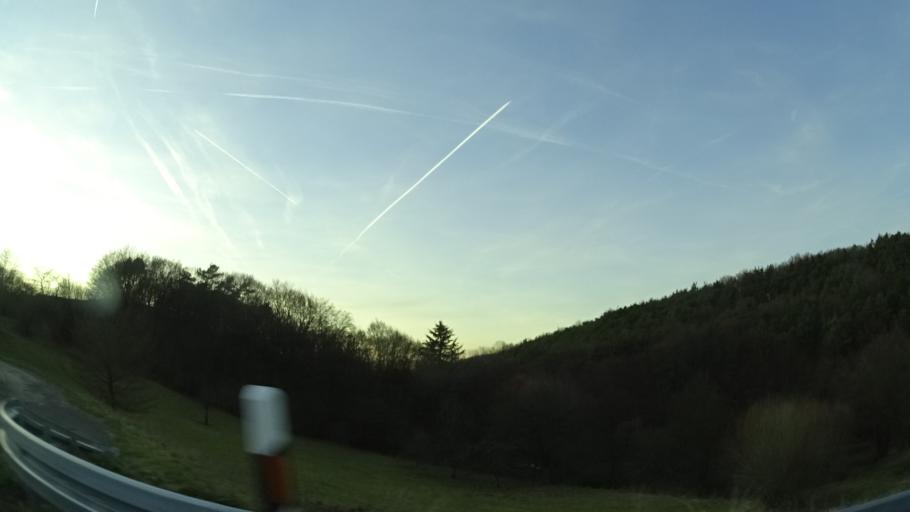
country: DE
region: Bavaria
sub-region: Regierungsbezirk Unterfranken
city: Mombris
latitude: 50.0870
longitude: 9.1575
